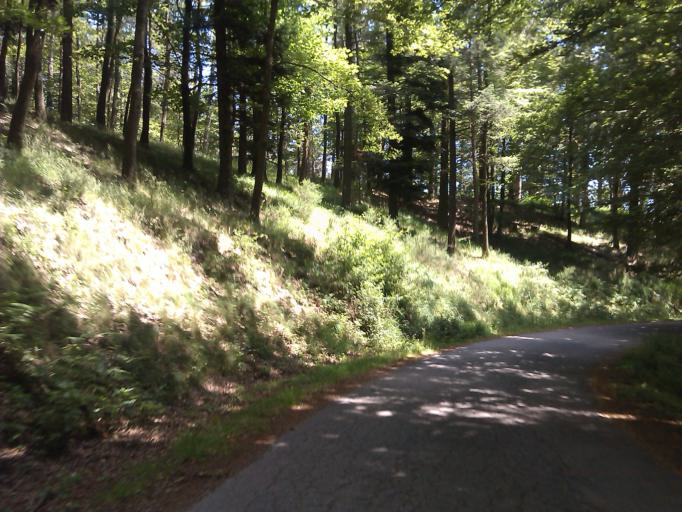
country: IT
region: Tuscany
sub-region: Provincia di Prato
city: Cantagallo
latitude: 43.9917
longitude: 11.0398
